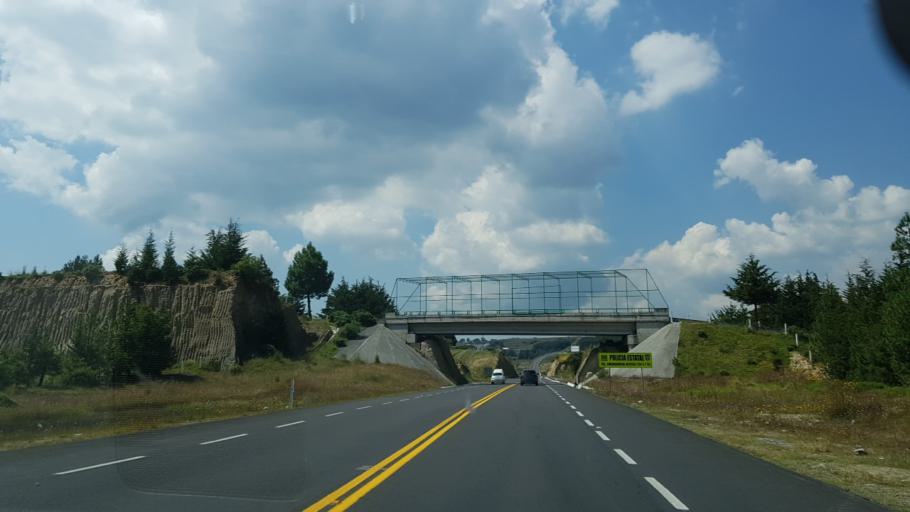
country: MX
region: Mexico
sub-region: Villa Victoria
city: Colonia Doctor Gustavo Baz
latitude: 19.3582
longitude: -99.9583
